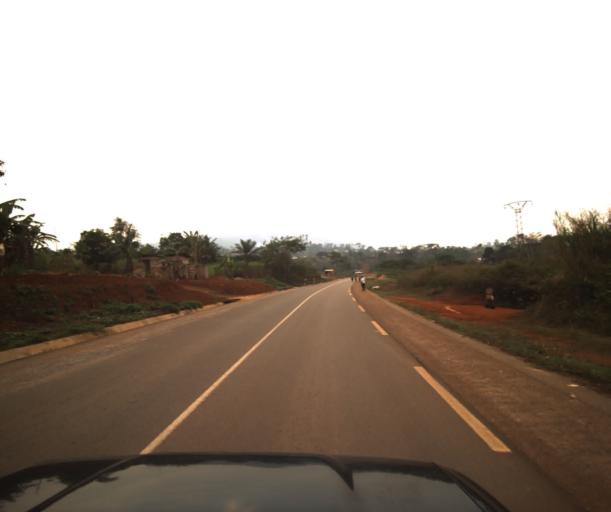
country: CM
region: Centre
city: Mbankomo
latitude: 3.7942
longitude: 11.4496
